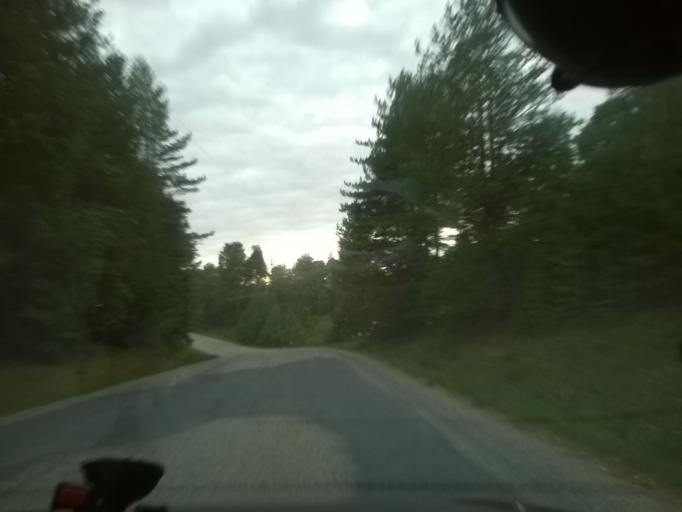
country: EE
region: Vorumaa
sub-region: Voru linn
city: Voru
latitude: 57.8104
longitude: 27.0890
